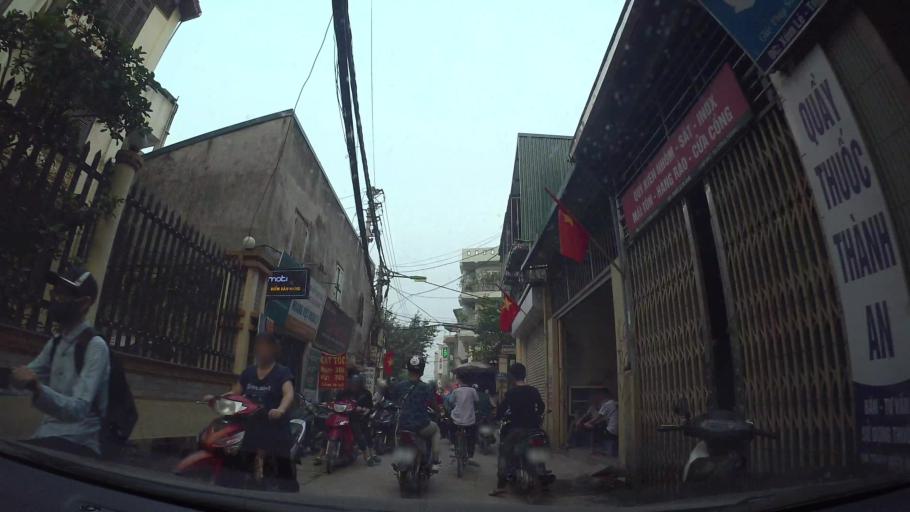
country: VN
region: Ha Noi
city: Thanh Xuan
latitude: 20.9800
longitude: 105.8050
